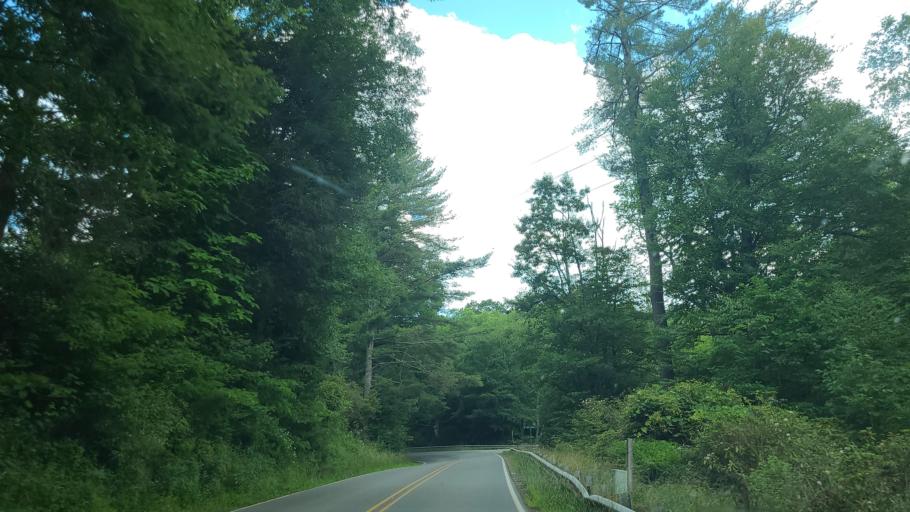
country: US
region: North Carolina
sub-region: Ashe County
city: Jefferson
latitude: 36.3914
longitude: -81.3652
